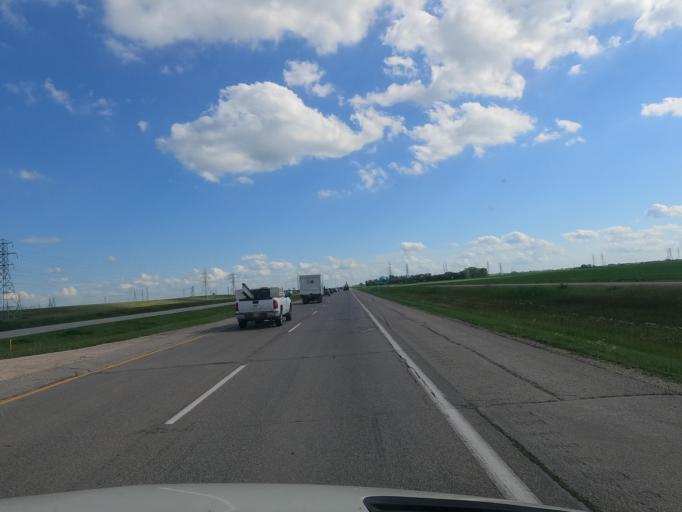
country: CA
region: Manitoba
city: Winnipeg
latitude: 49.8773
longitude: -96.9592
